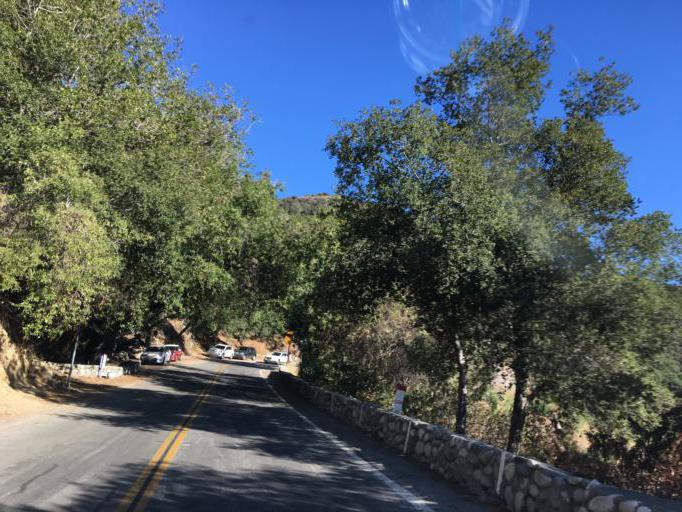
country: US
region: California
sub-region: Los Angeles County
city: Sierra Madre
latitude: 34.1949
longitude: -118.0220
